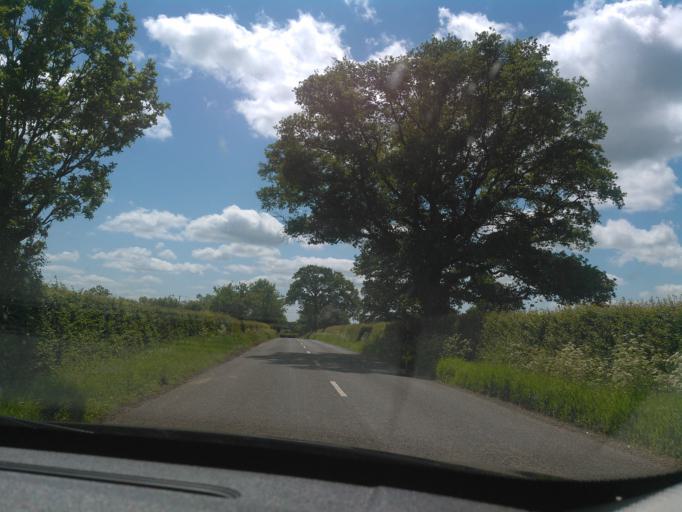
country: GB
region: England
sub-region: Shropshire
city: Wem
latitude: 52.8705
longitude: -2.7190
